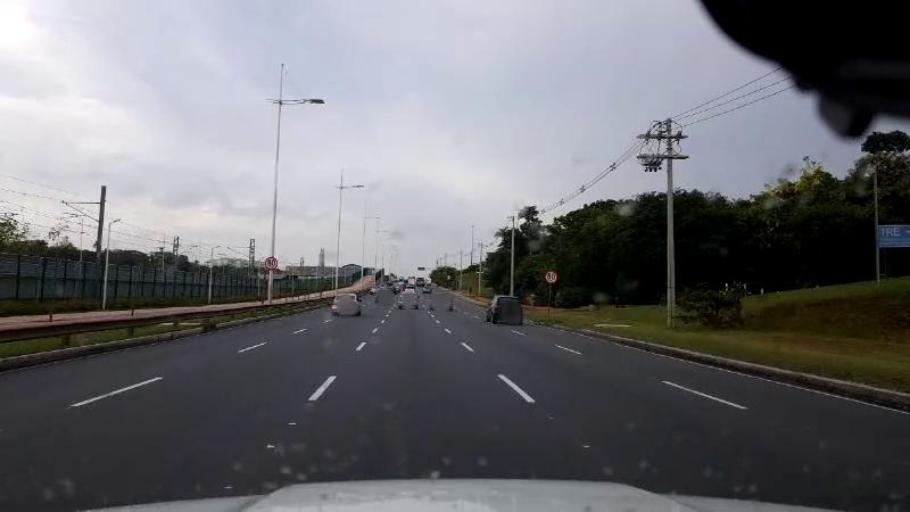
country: BR
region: Bahia
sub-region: Salvador
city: Salvador
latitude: -12.9518
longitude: -38.4265
